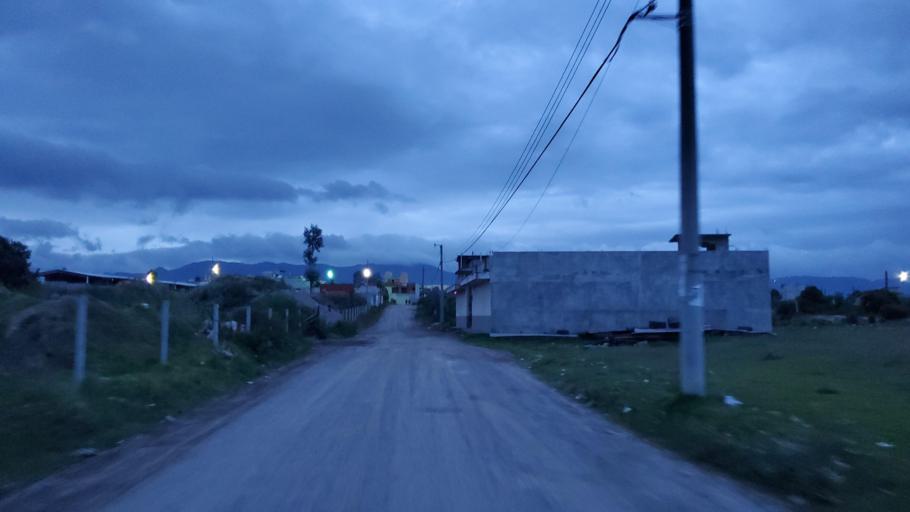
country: GT
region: Quetzaltenango
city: Quetzaltenango
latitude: 14.8285
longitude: -91.5393
